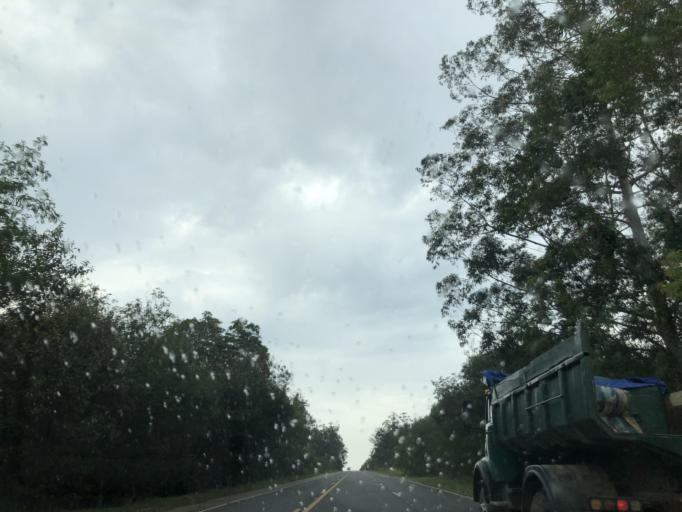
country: BR
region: Sao Paulo
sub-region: Salto De Pirapora
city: Salto de Pirapora
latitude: -23.6773
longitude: -47.6037
